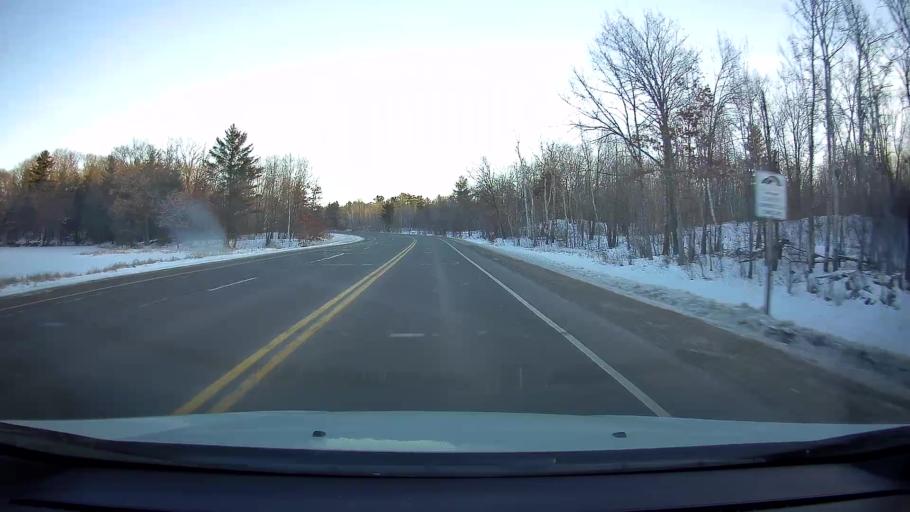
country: US
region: Wisconsin
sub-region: Barron County
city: Turtle Lake
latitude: 45.4530
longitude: -92.1042
